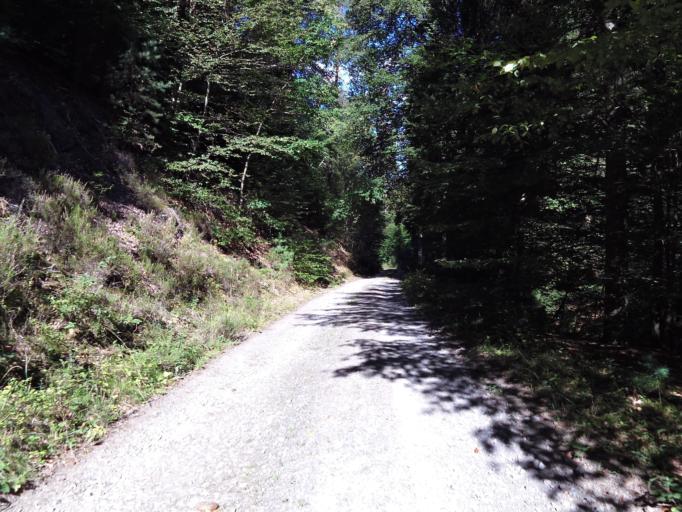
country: DE
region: Rheinland-Pfalz
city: Neidenfels
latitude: 49.4333
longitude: 8.0422
